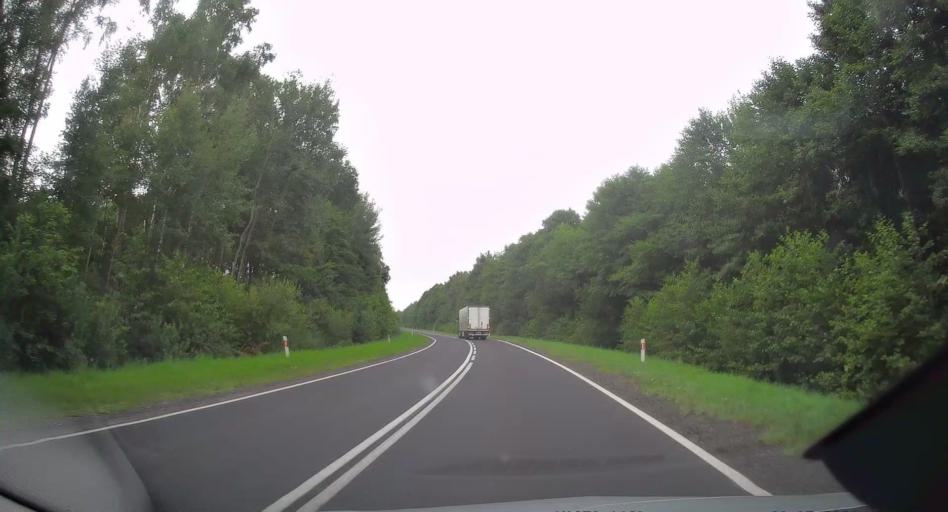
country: PL
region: Lodz Voivodeship
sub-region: Powiat radomszczanski
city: Radomsko
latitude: 51.0222
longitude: 19.4329
